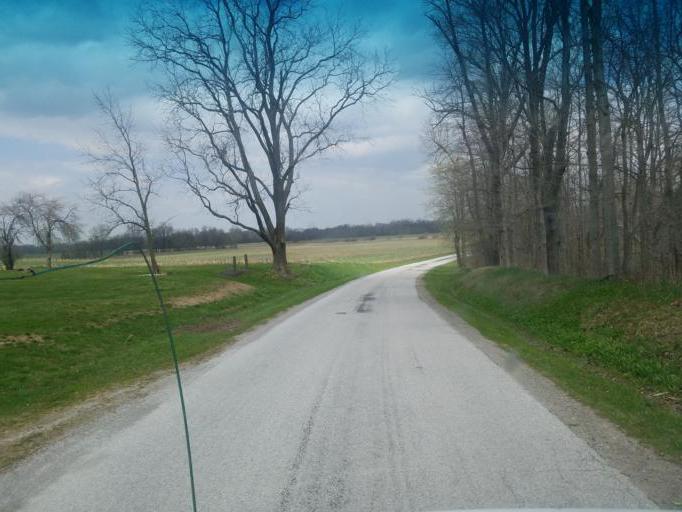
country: US
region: Ohio
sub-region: Wyandot County
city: Upper Sandusky
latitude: 40.9203
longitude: -83.2545
